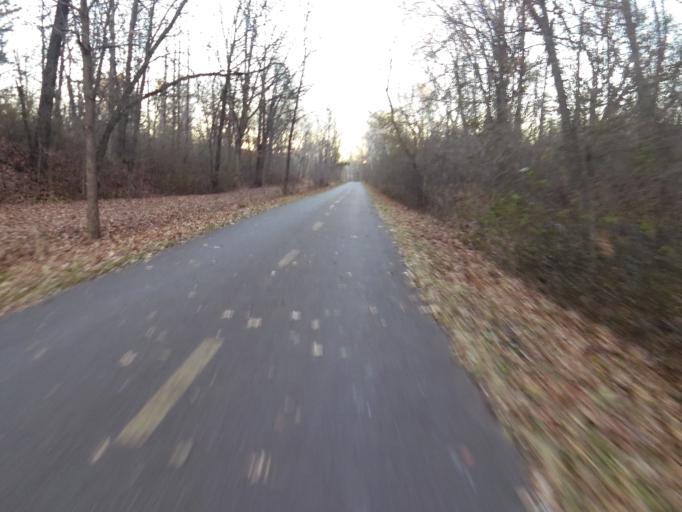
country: US
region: Minnesota
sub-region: Washington County
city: Grant
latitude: 45.0775
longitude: -92.8994
